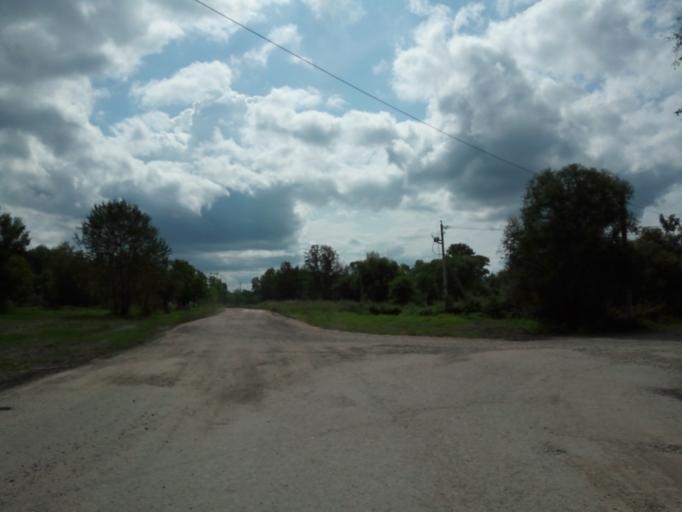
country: RU
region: Primorskiy
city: Dal'nerechensk
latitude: 45.9497
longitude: 133.8243
